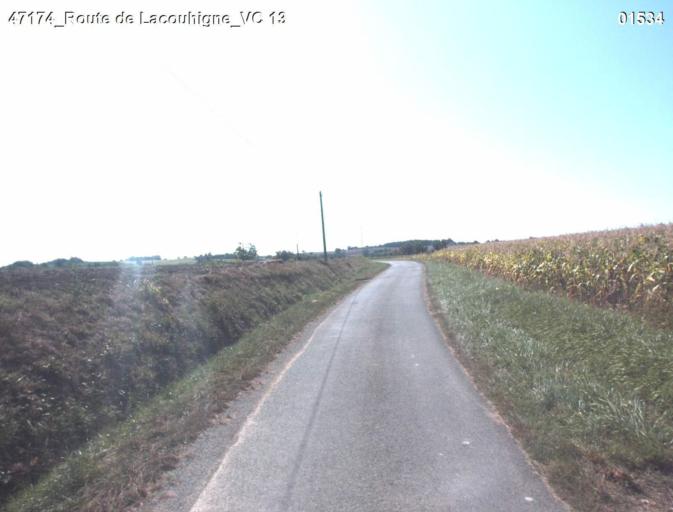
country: FR
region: Midi-Pyrenees
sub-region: Departement du Gers
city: Condom
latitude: 44.0255
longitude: 0.3772
